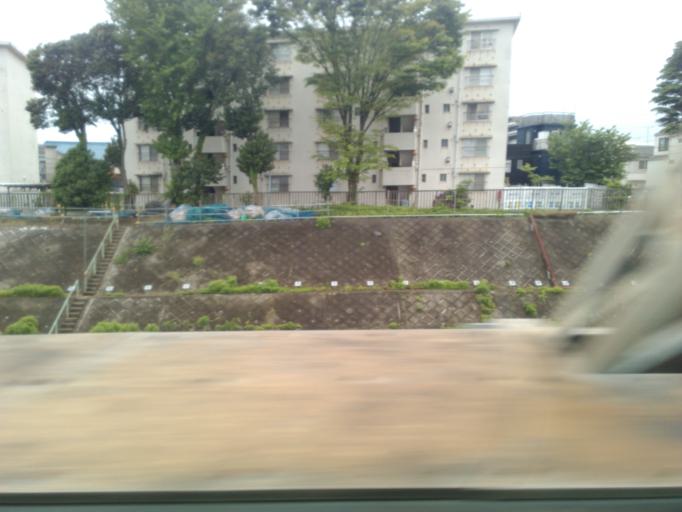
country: JP
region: Saitama
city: Kawaguchi
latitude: 35.7435
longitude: 139.7530
